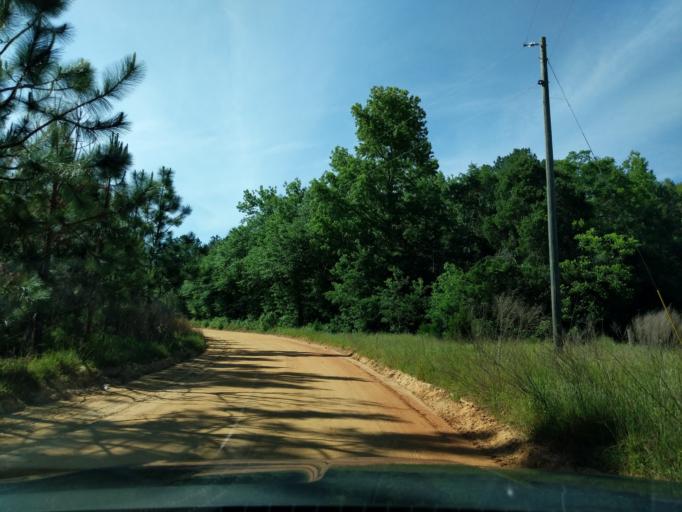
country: US
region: Georgia
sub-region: Jefferson County
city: Wrens
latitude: 33.2283
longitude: -82.3514
